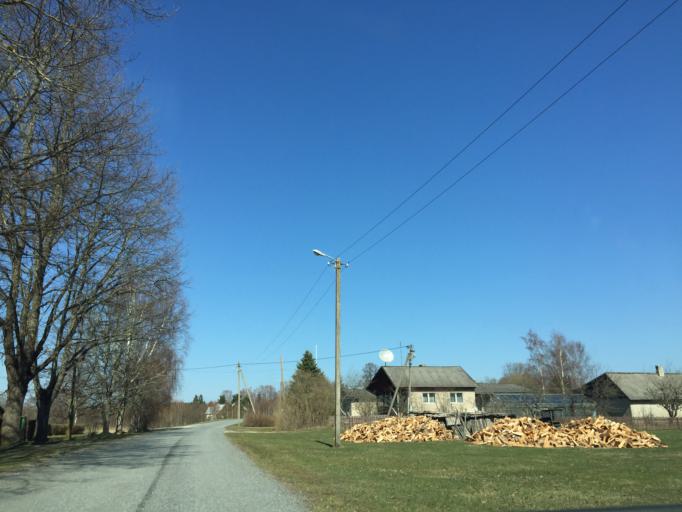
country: EE
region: Jogevamaa
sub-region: Mustvee linn
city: Mustvee
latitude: 58.9505
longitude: 27.0493
